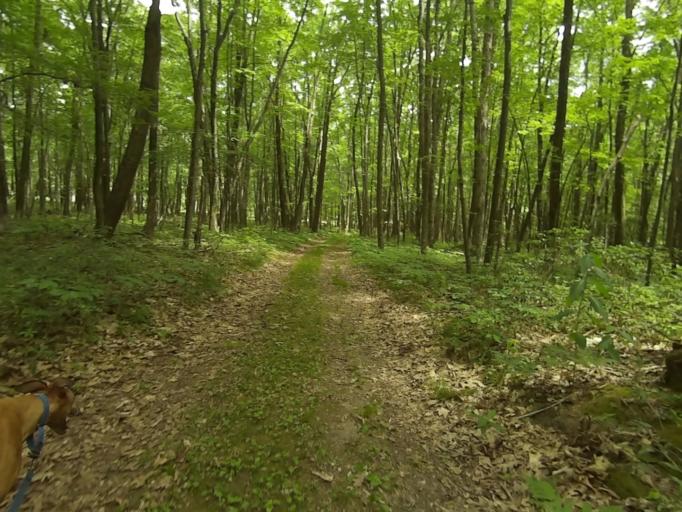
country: US
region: Pennsylvania
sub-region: Centre County
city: Stormstown
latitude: 40.9138
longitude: -78.0561
